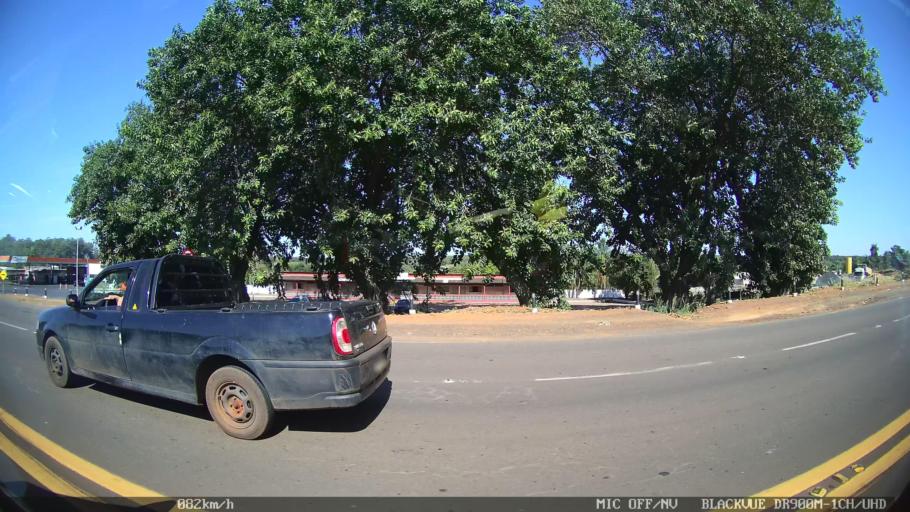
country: BR
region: Sao Paulo
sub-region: Batatais
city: Batatais
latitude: -20.9045
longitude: -47.6004
